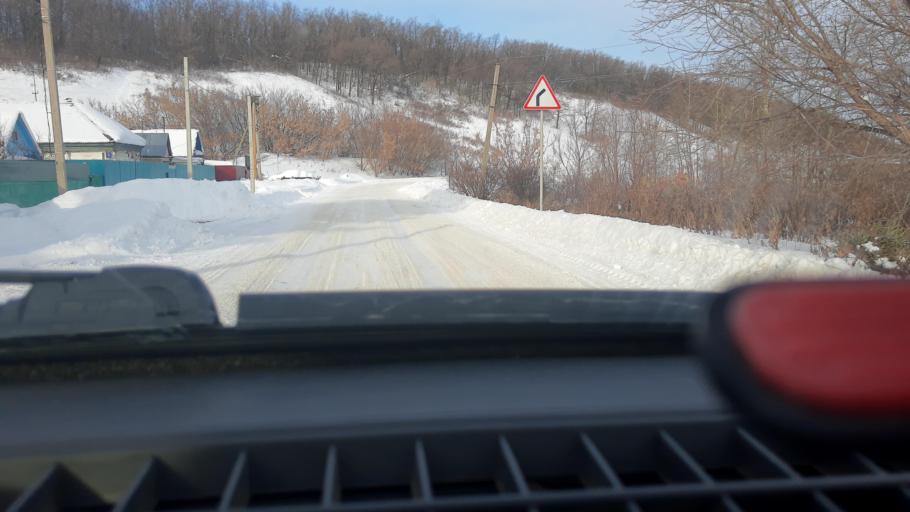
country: RU
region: Bashkortostan
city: Ufa
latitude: 54.5228
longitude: 55.9091
